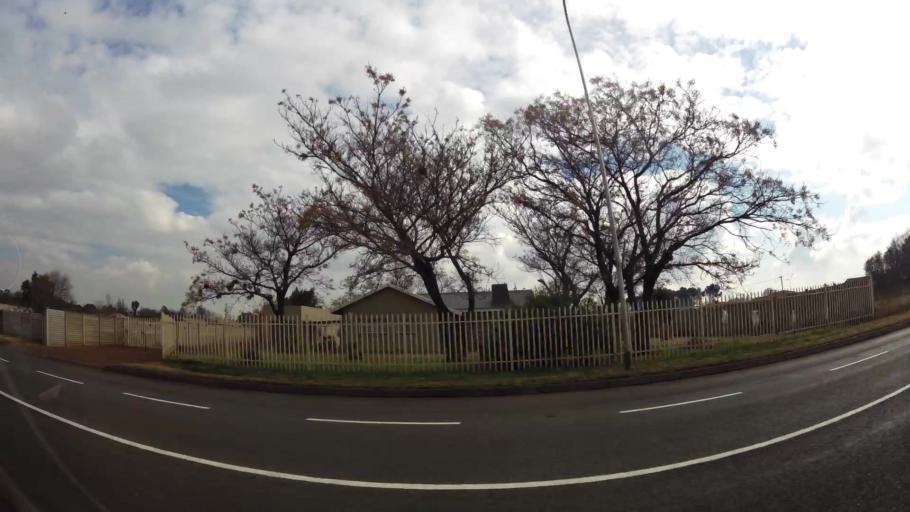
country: ZA
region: Gauteng
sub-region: Sedibeng District Municipality
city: Meyerton
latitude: -26.5918
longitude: 27.9983
